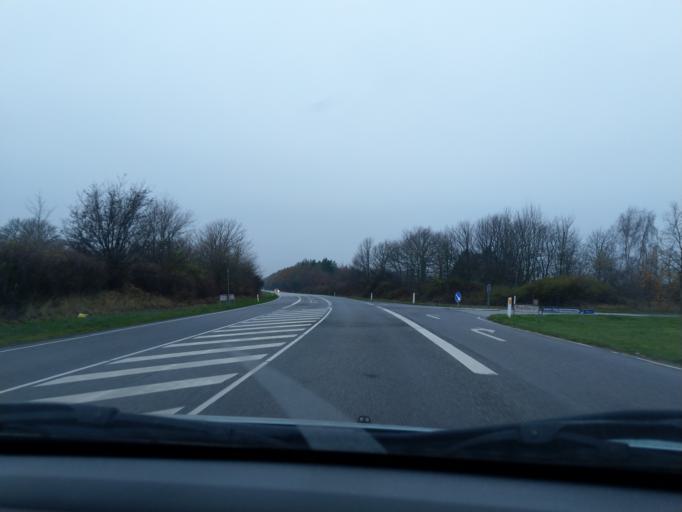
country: DK
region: Zealand
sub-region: Vordingborg Kommune
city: Praesto
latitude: 55.1125
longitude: 12.0603
